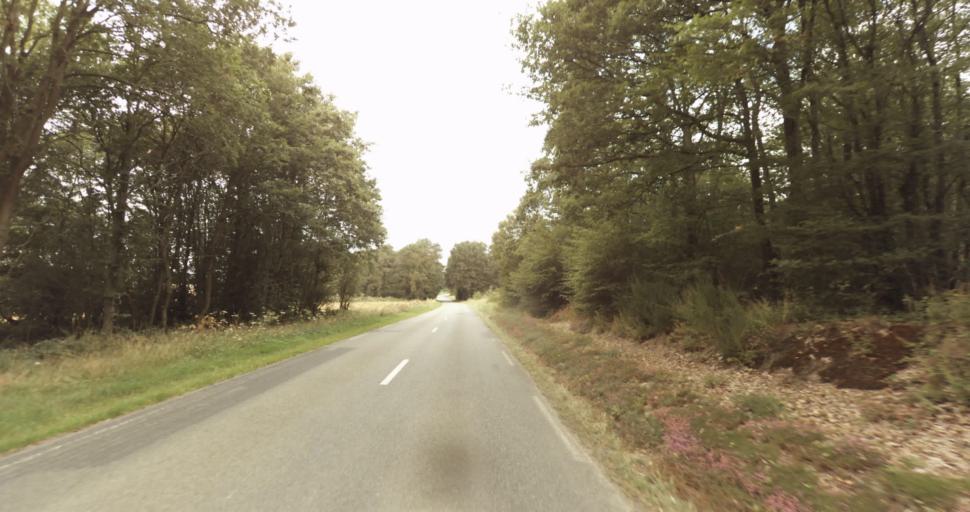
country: FR
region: Haute-Normandie
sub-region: Departement de l'Eure
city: Menilles
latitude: 48.9804
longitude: 1.2734
